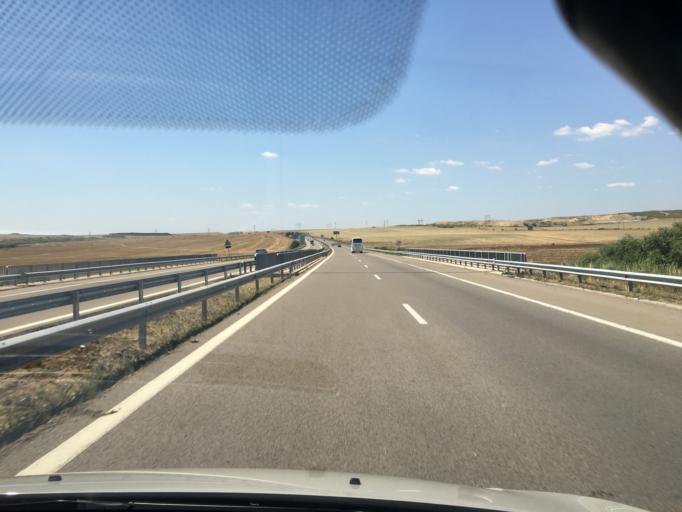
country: BG
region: Burgas
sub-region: Obshtina Kameno
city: Kameno
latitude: 42.6046
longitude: 27.2908
